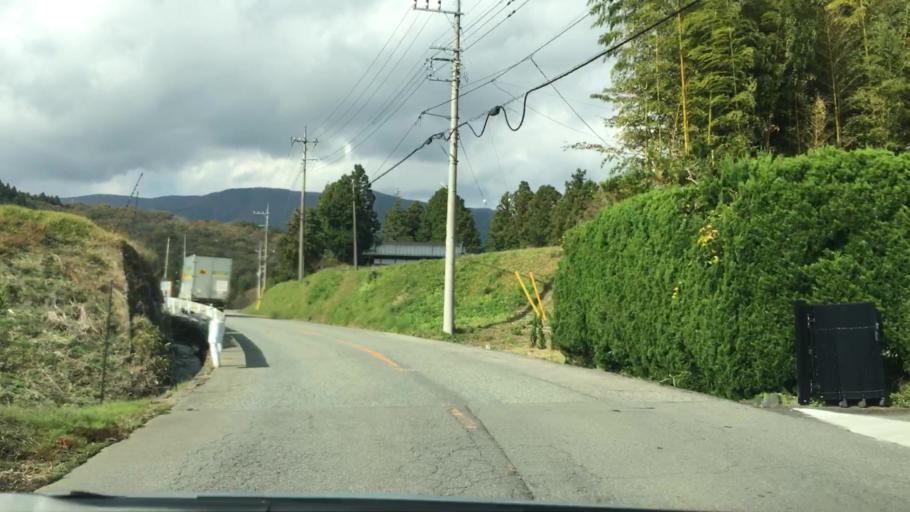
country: JP
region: Shizuoka
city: Gotemba
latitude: 35.3725
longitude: 138.9472
